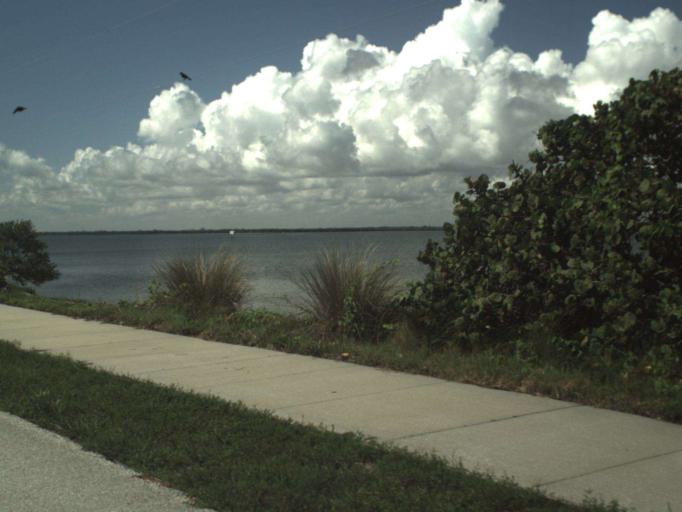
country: US
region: Florida
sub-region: Indian River County
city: Sebastian
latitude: 27.8360
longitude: -80.4358
